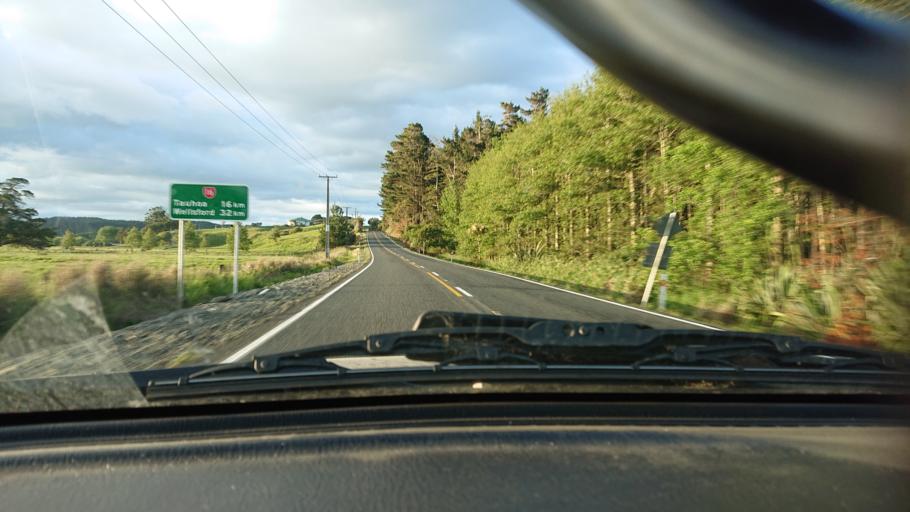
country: NZ
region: Auckland
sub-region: Auckland
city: Parakai
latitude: -36.5045
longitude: 174.4557
